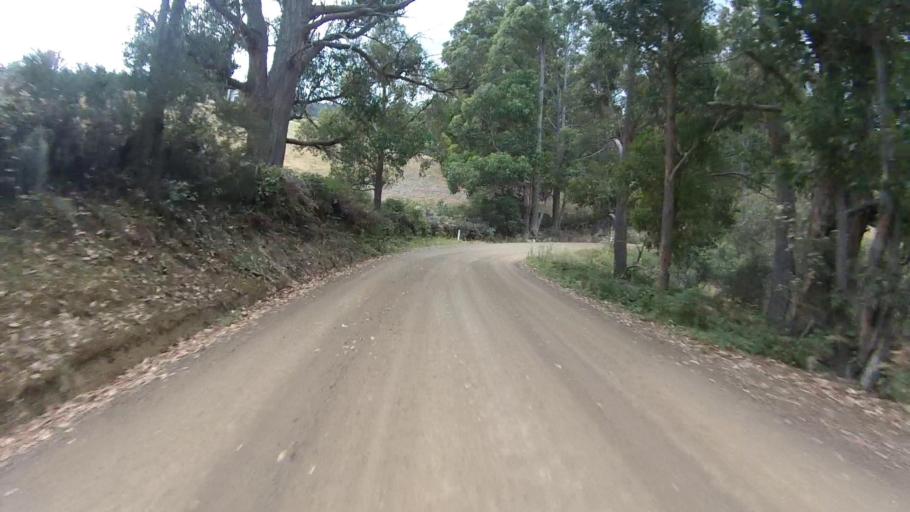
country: AU
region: Tasmania
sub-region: Huon Valley
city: Huonville
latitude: -42.9707
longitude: 147.0608
